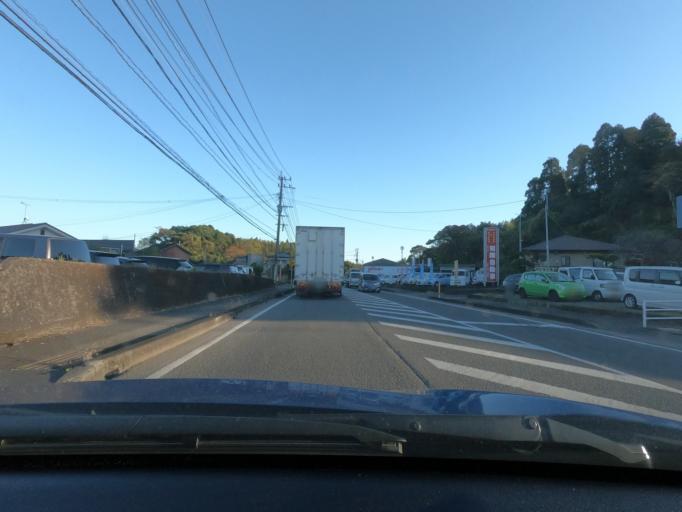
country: JP
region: Kagoshima
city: Satsumasendai
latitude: 31.8420
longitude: 130.2812
